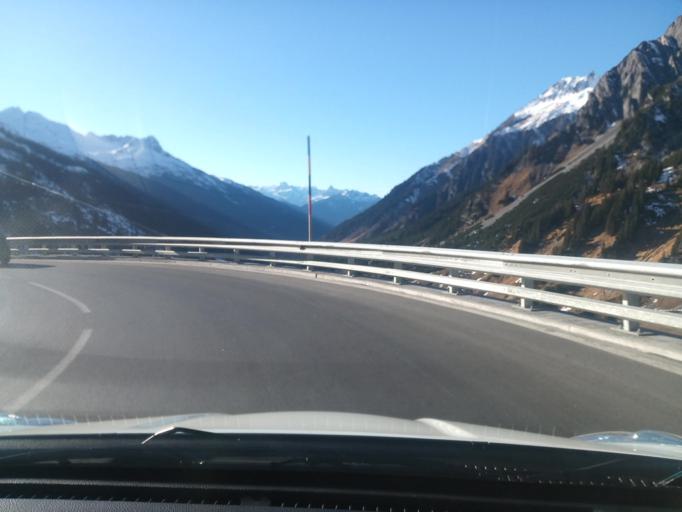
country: AT
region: Vorarlberg
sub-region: Politischer Bezirk Bludenz
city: Lech
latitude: 47.1408
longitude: 10.1659
